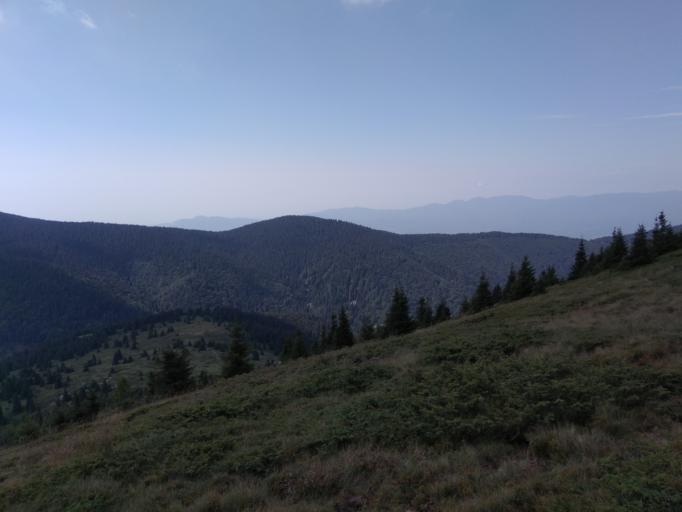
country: BG
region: Plovdiv
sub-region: Obshtina Karlovo
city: Karlovo
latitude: 42.7294
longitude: 24.7502
